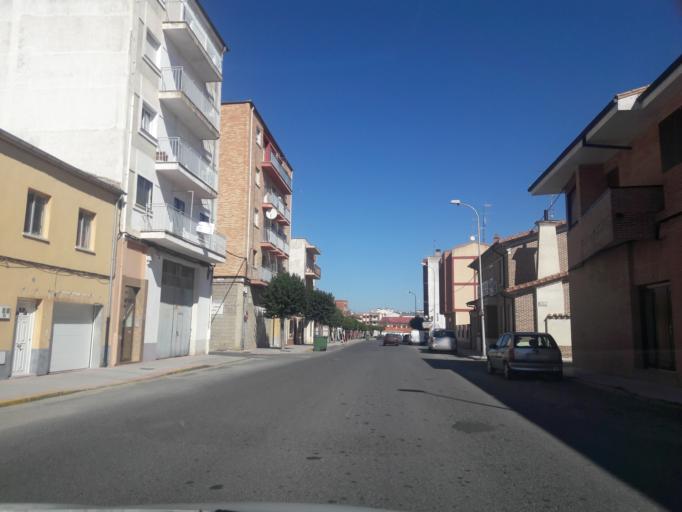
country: ES
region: Castille and Leon
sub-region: Provincia de Salamanca
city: Penaranda de Bracamonte
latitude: 40.8961
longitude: -5.2003
